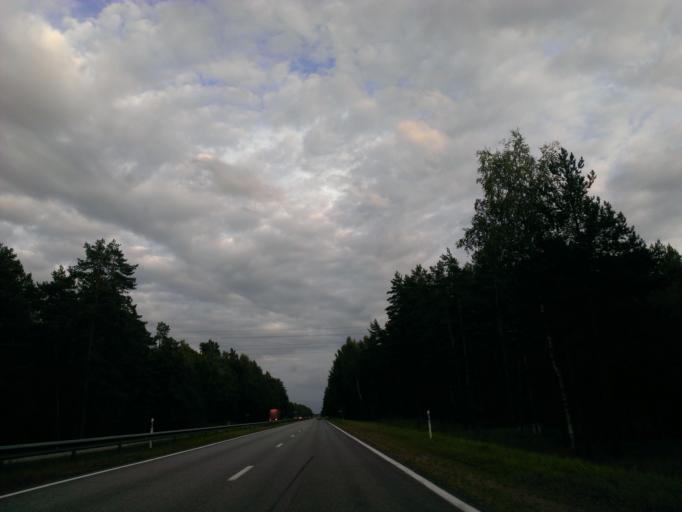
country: LV
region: Ikskile
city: Ikskile
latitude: 56.8328
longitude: 24.5078
